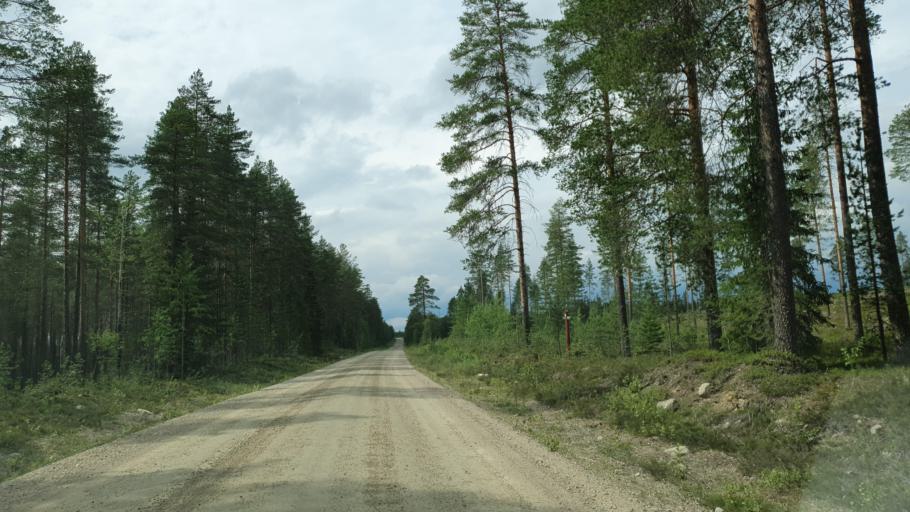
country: FI
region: Kainuu
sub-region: Kehys-Kainuu
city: Kuhmo
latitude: 64.7231
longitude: 29.6843
